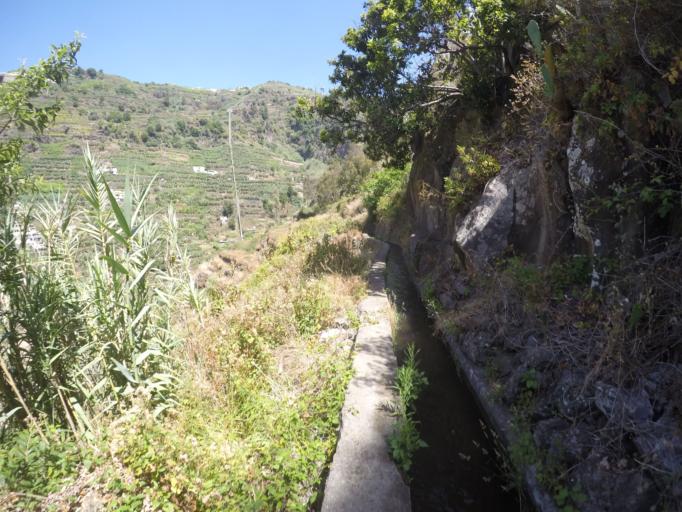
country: PT
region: Madeira
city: Camara de Lobos
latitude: 32.6663
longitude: -16.9588
